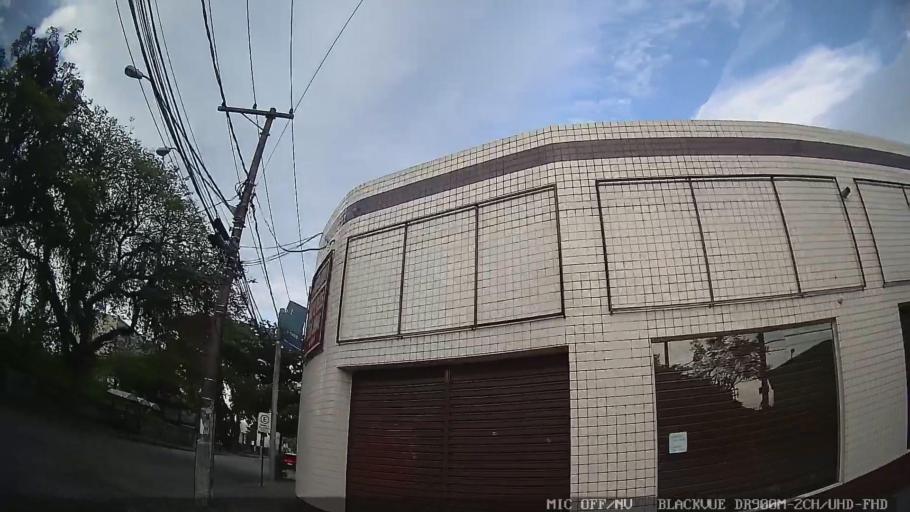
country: BR
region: Sao Paulo
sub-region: Cubatao
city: Cubatao
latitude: -23.8913
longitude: -46.4224
